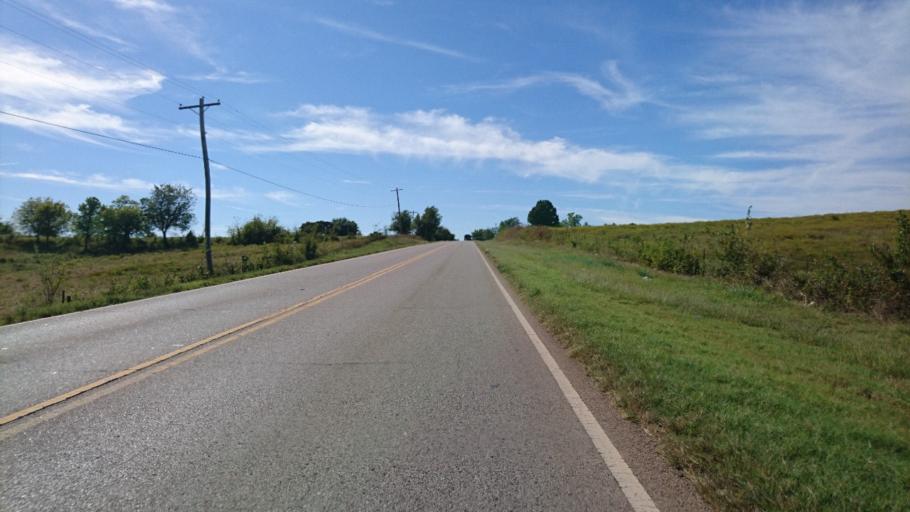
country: US
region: Oklahoma
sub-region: Lincoln County
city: Chandler
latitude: 35.7099
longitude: -96.8094
